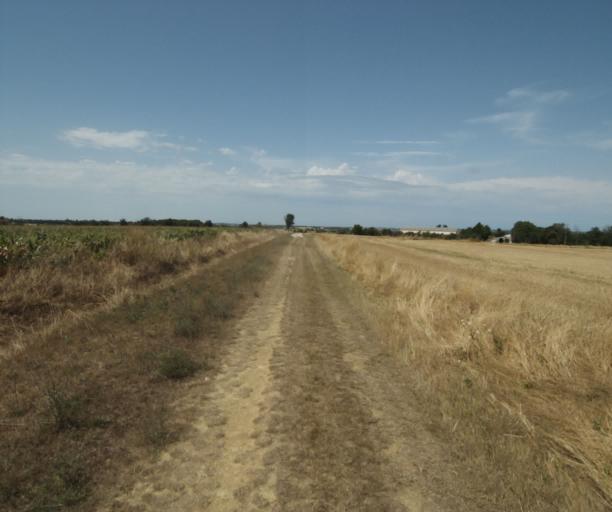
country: FR
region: Midi-Pyrenees
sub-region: Departement de la Haute-Garonne
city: Saint-Felix-Lauragais
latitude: 43.4517
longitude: 1.8565
